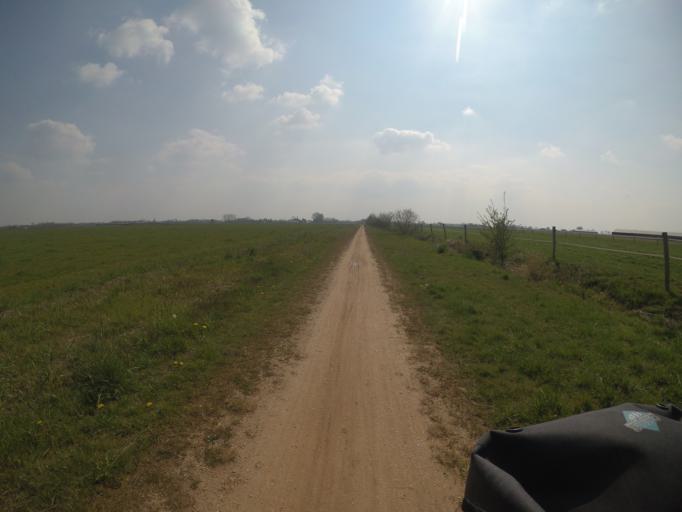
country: NL
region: Gelderland
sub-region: Gemeente Druten
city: Druten
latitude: 51.8611
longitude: 5.5507
